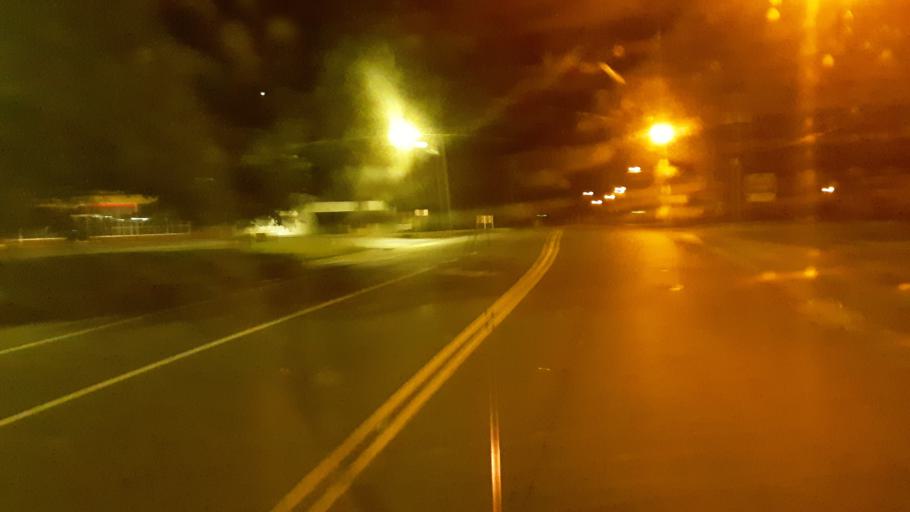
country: US
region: New York
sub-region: Oneida County
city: Rome
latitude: 43.2303
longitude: -75.4394
